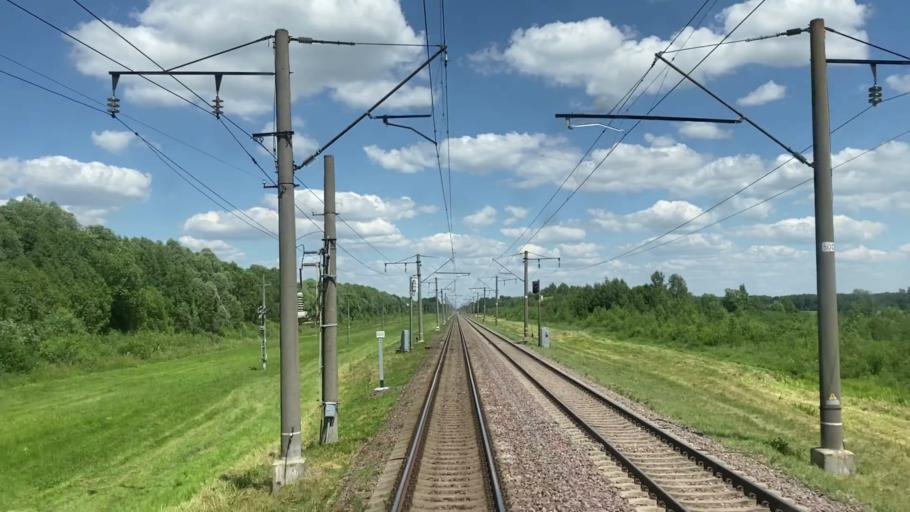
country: BY
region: Brest
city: Zhabinka
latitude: 52.2187
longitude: 24.0584
